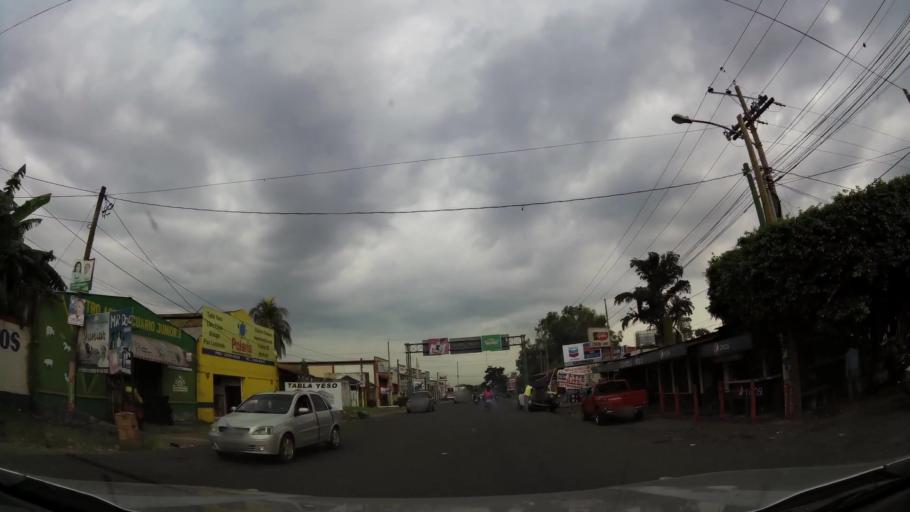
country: GT
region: Escuintla
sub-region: Municipio de Escuintla
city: Escuintla
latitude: 14.2919
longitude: -90.7830
